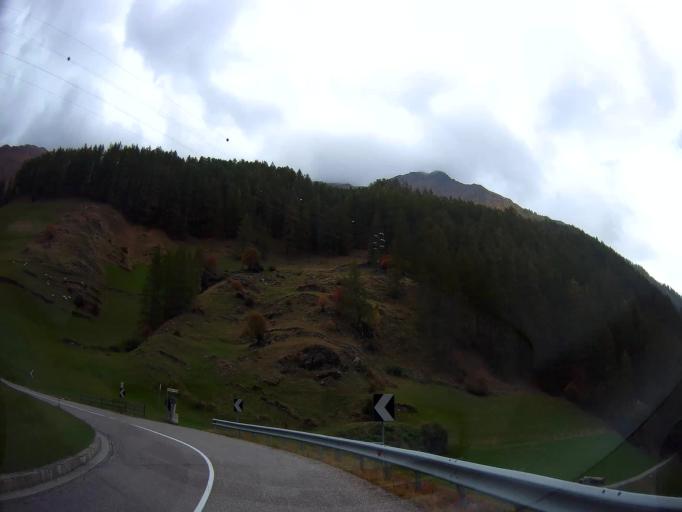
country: IT
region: Trentino-Alto Adige
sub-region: Bolzano
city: Senales
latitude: 46.7311
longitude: 10.8535
